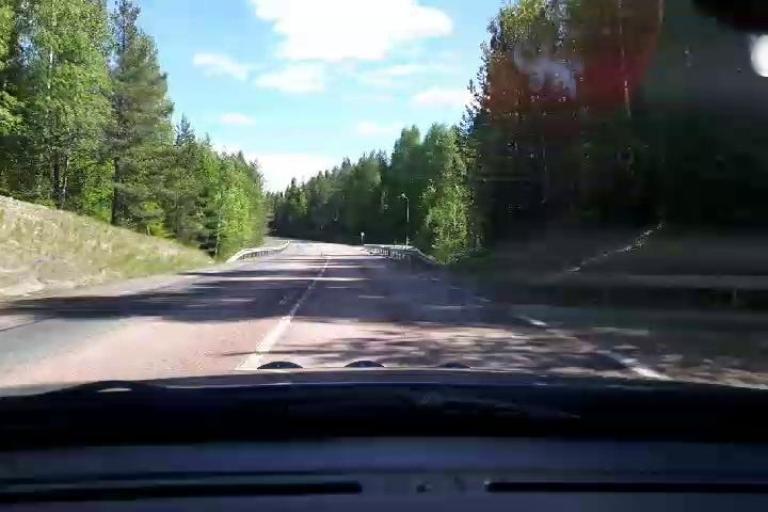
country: SE
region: Gaevleborg
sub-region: Ljusdals Kommun
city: Farila
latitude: 61.8882
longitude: 15.6764
